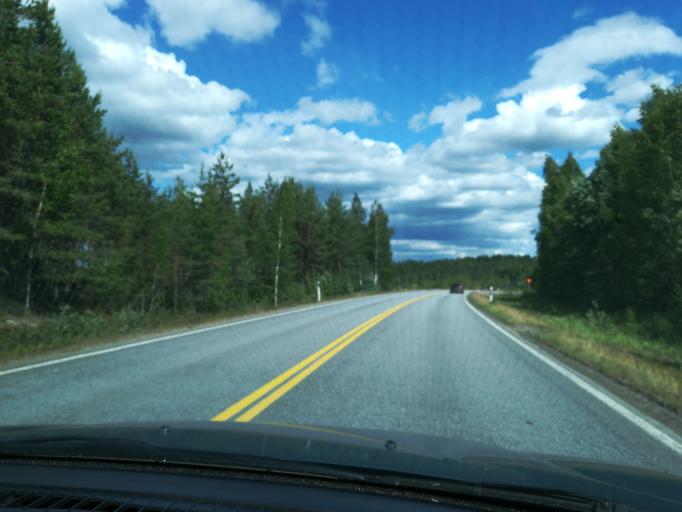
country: FI
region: Southern Savonia
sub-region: Mikkeli
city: Hirvensalmi
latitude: 61.6610
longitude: 26.9525
